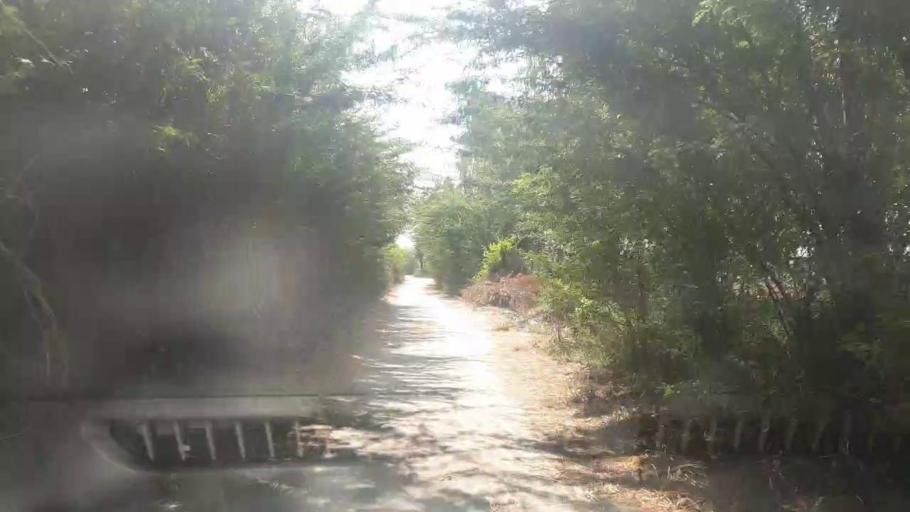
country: PK
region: Sindh
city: Badin
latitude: 24.6313
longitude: 68.9129
